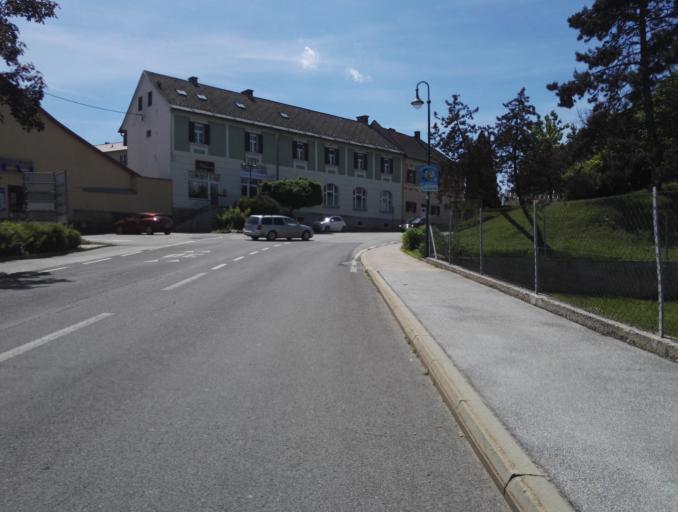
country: AT
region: Styria
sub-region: Politischer Bezirk Graz-Umgebung
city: Kalsdorf bei Graz
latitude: 46.9646
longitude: 15.4798
